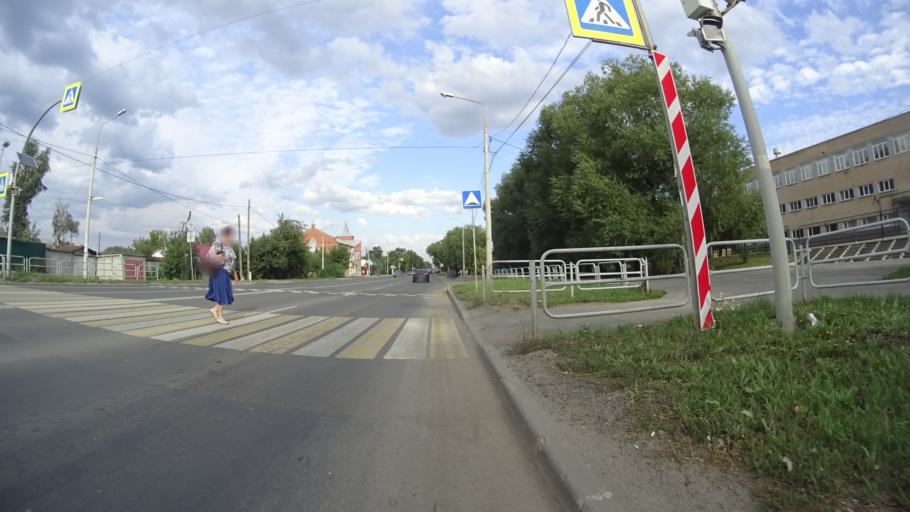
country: RU
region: Chelyabinsk
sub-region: Gorod Chelyabinsk
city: Chelyabinsk
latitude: 55.1985
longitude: 61.3413
